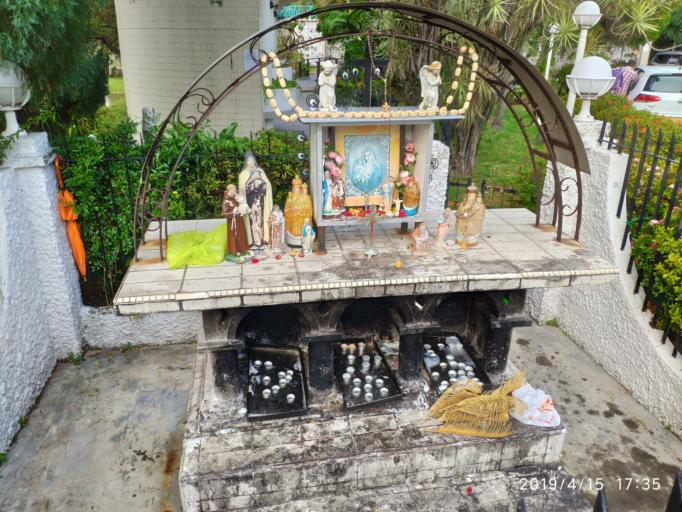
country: SG
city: Singapore
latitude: 1.2735
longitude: 103.8282
